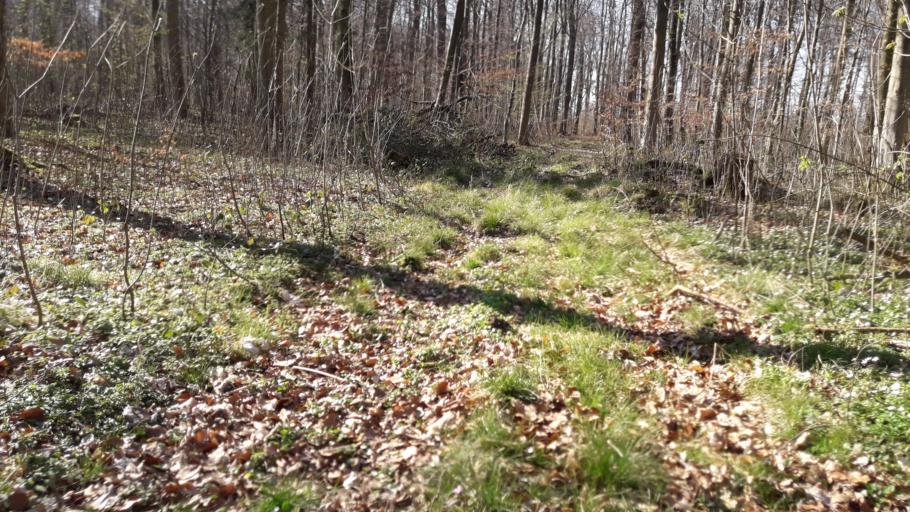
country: DE
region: North Rhine-Westphalia
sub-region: Regierungsbezirk Detmold
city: Paderborn
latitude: 51.6794
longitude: 8.6835
